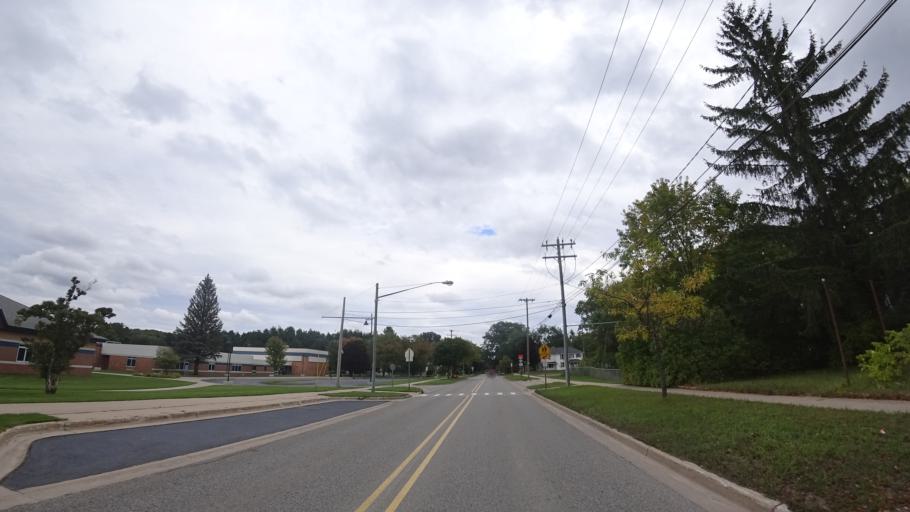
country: US
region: Michigan
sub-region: Emmet County
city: Harbor Springs
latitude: 45.4353
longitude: -84.9893
